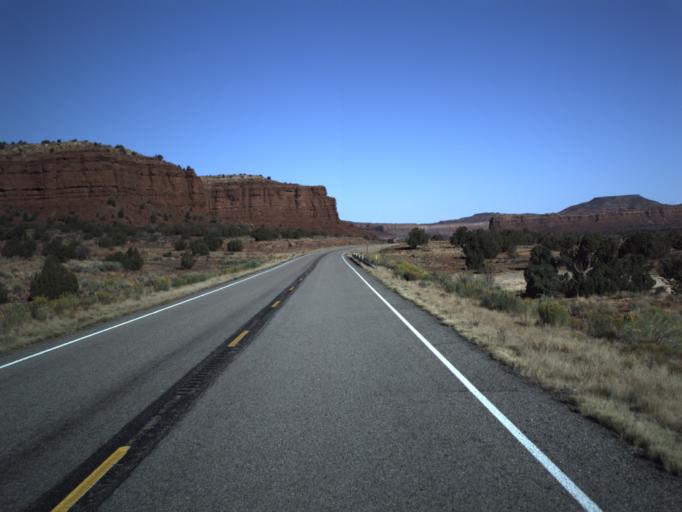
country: US
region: Utah
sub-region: San Juan County
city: Blanding
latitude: 37.6818
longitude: -110.2193
